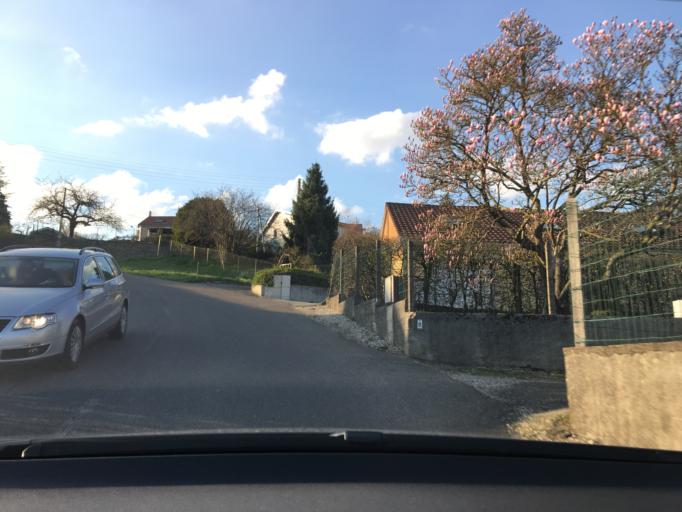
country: FR
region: Franche-Comte
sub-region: Departement du Doubs
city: Bavans
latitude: 47.4825
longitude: 6.7343
